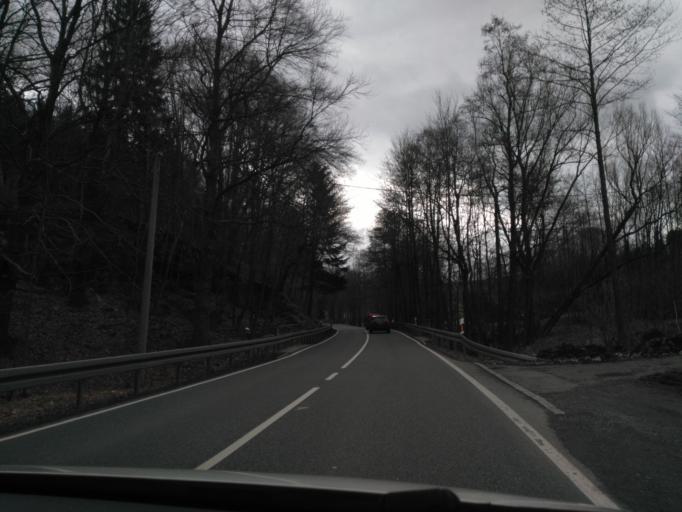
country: DE
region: Saxony
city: Wolkenstein
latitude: 50.6628
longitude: 13.0738
